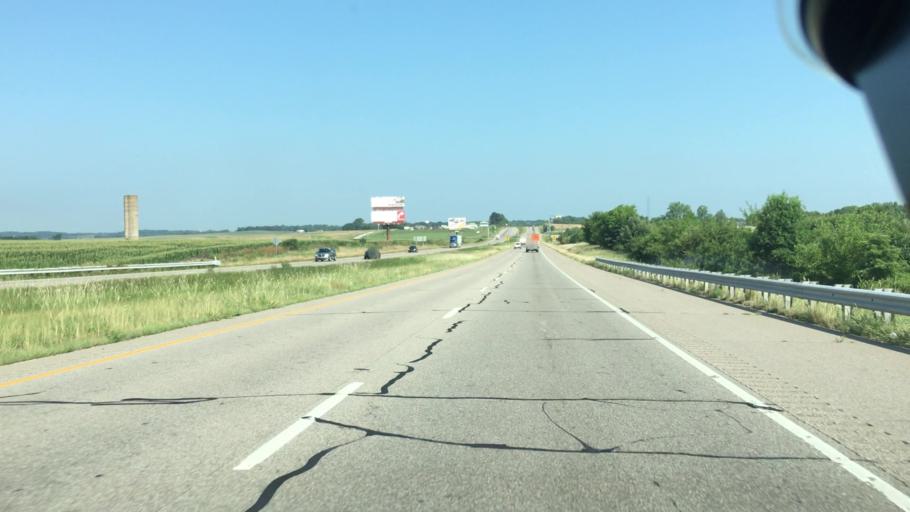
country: US
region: Indiana
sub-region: Gibson County
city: Princeton
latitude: 38.3218
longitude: -87.5778
